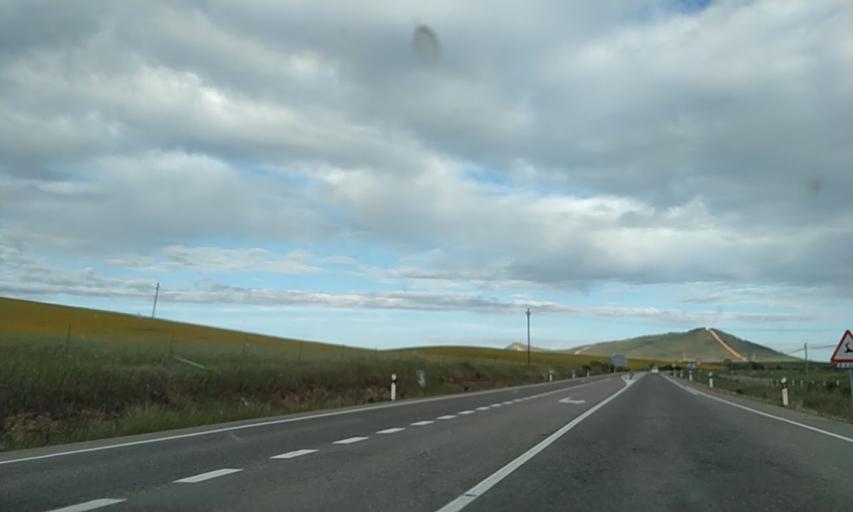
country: ES
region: Extremadura
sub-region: Provincia de Caceres
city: Pedroso de Acim
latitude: 39.8412
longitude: -6.4000
